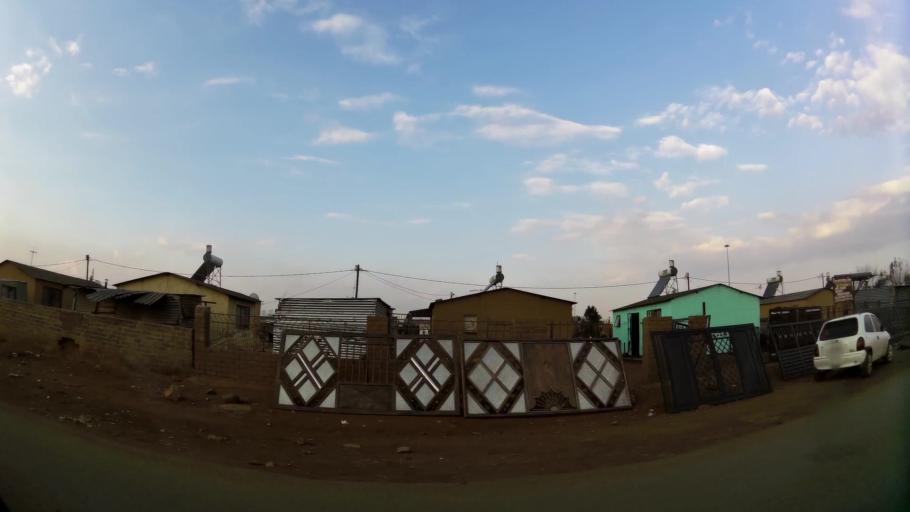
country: ZA
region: Gauteng
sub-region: City of Johannesburg Metropolitan Municipality
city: Orange Farm
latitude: -26.5583
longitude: 27.8312
